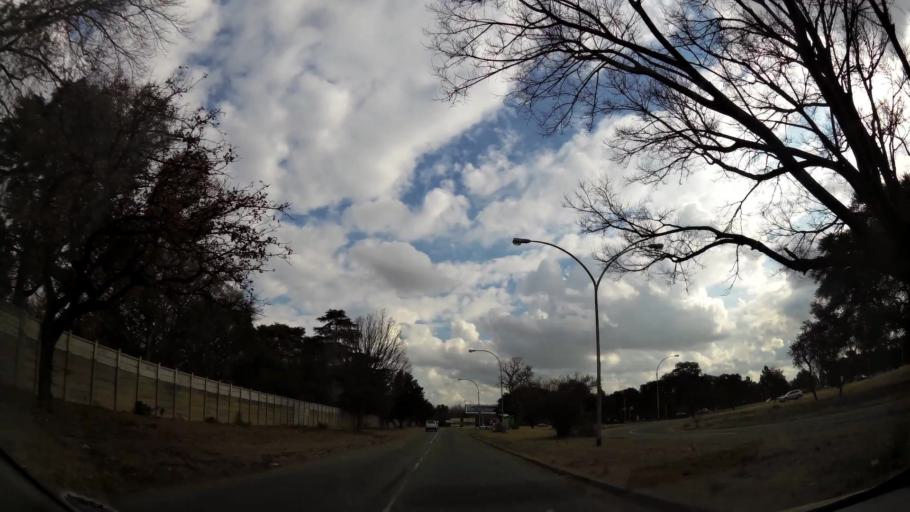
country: ZA
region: Orange Free State
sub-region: Fezile Dabi District Municipality
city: Sasolburg
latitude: -26.8041
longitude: 27.8317
